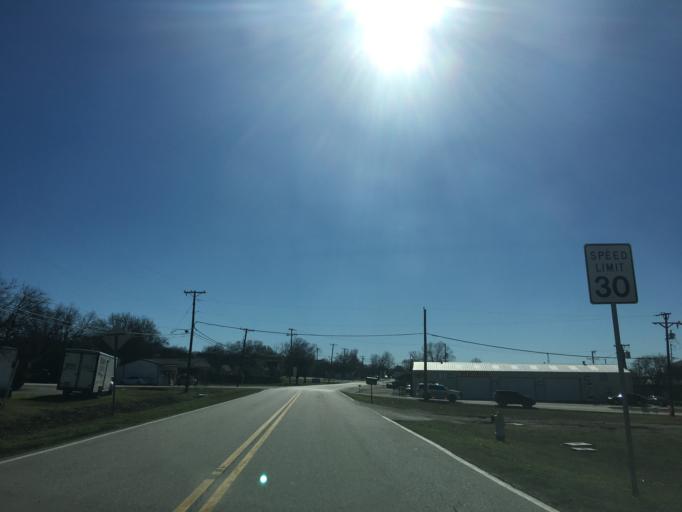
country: US
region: Texas
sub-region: Collin County
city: Prosper
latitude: 33.2378
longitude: -96.8021
